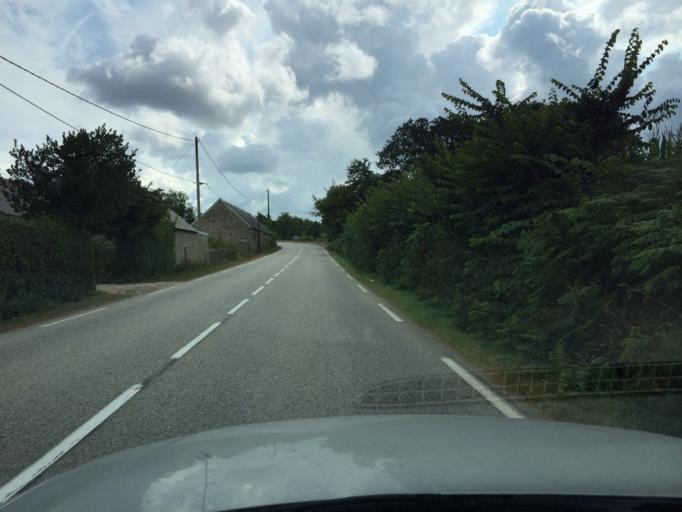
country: FR
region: Lower Normandy
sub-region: Departement de la Manche
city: Tollevast
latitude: 49.5602
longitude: -1.6130
